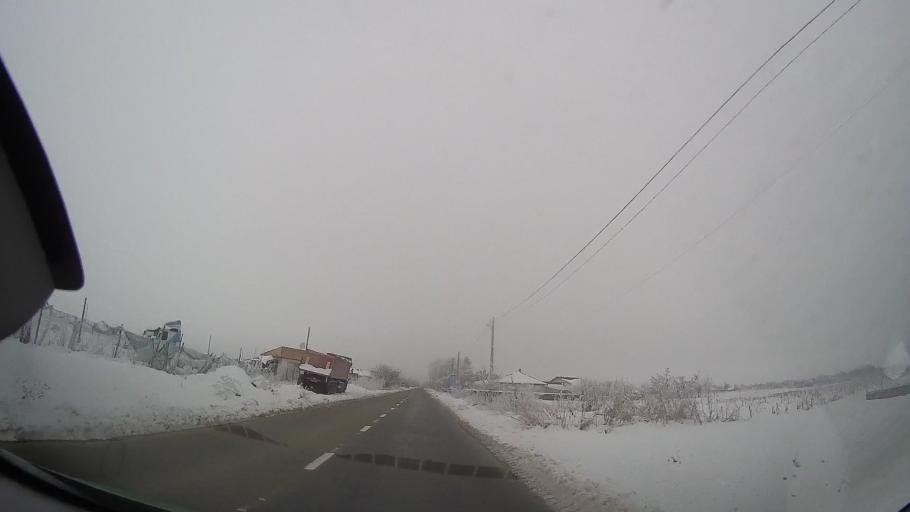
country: RO
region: Neamt
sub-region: Comuna Horia
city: Cotu Vames
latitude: 46.8953
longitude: 26.9605
